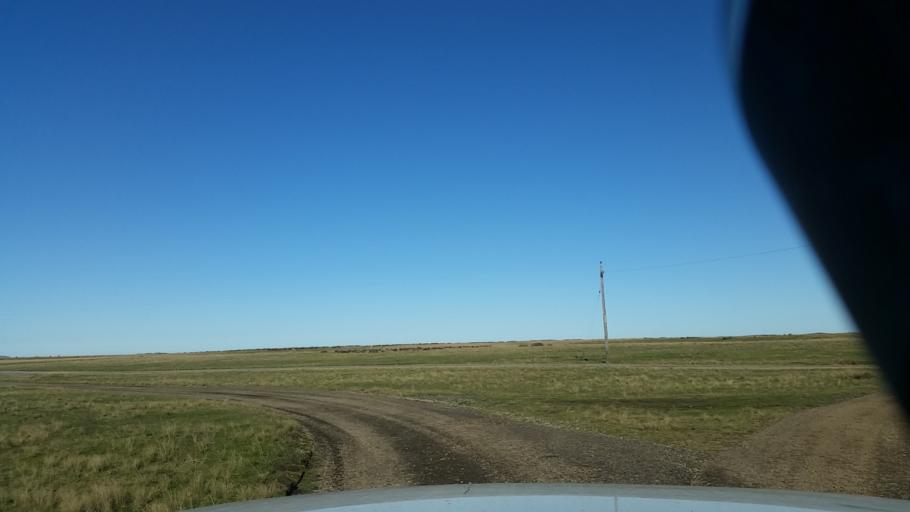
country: NZ
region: Canterbury
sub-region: Selwyn District
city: Lincoln
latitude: -43.8144
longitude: 172.6373
